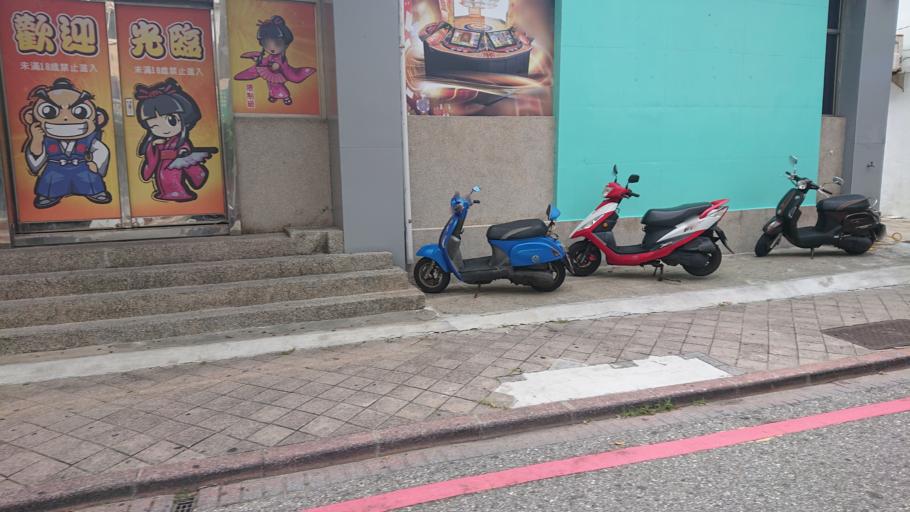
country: TW
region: Taiwan
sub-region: Penghu
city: Ma-kung
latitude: 23.5646
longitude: 119.5674
